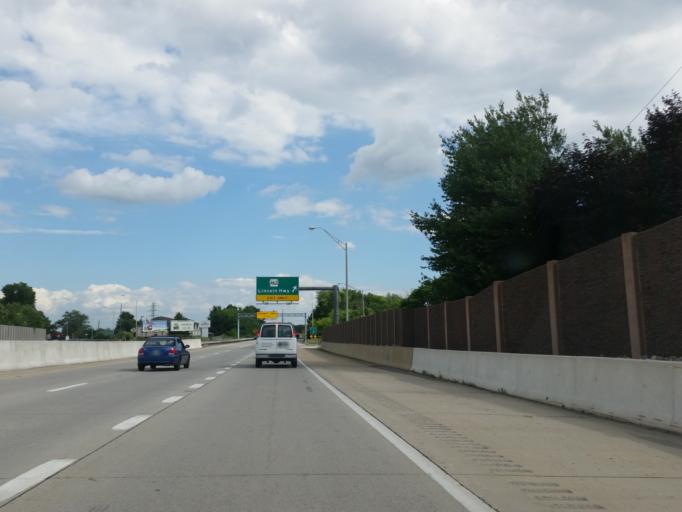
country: US
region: Pennsylvania
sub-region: Lancaster County
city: Lampeter
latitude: 40.0355
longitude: -76.2432
